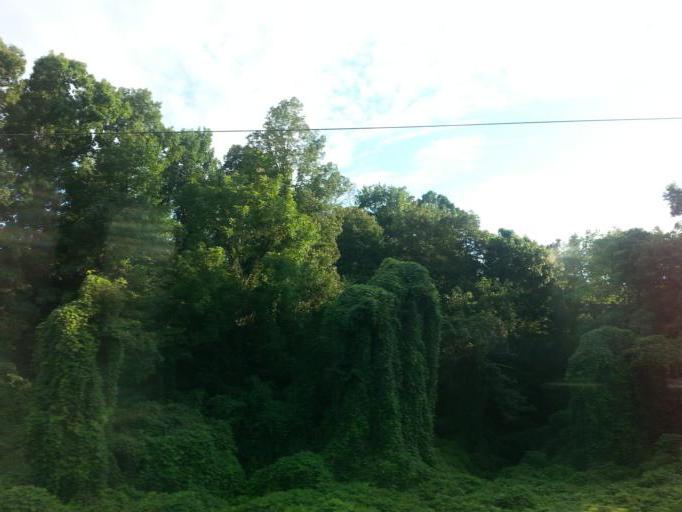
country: US
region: Alabama
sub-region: Lauderdale County
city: Rogersville
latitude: 34.8515
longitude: -87.4012
